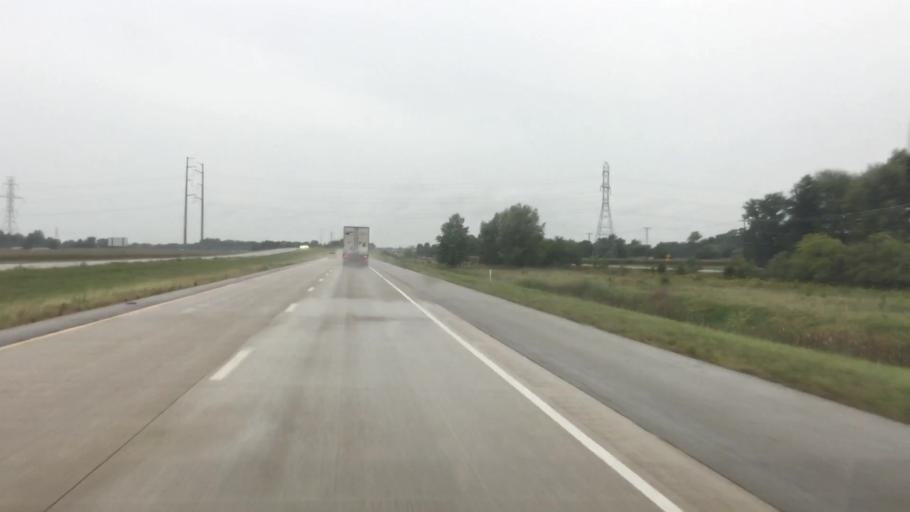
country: US
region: Indiana
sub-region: Allen County
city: New Haven
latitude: 41.0996
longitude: -84.9692
